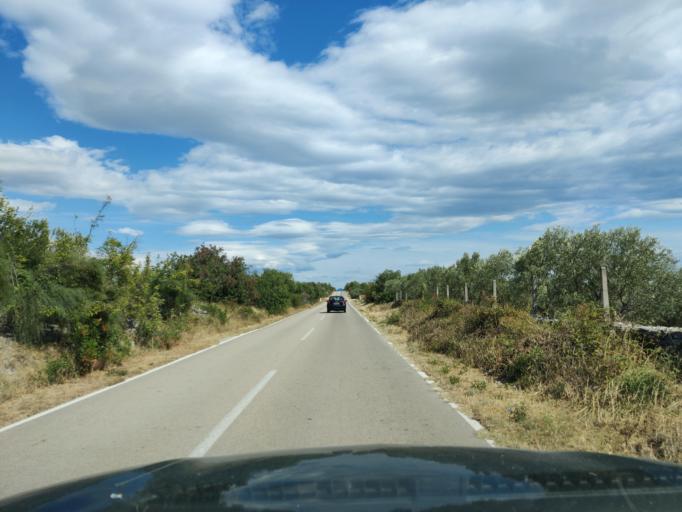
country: HR
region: Sibensko-Kniniska
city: Zaton
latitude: 43.7545
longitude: 15.8327
